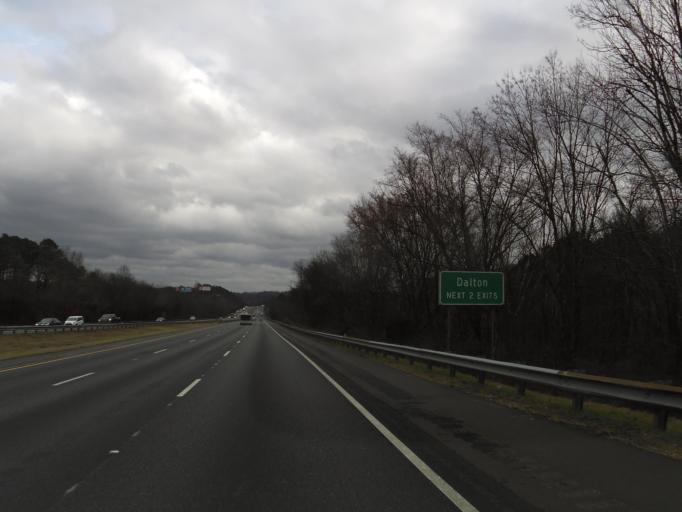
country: US
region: Georgia
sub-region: Whitfield County
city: Dalton
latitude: 34.8045
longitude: -85.0146
